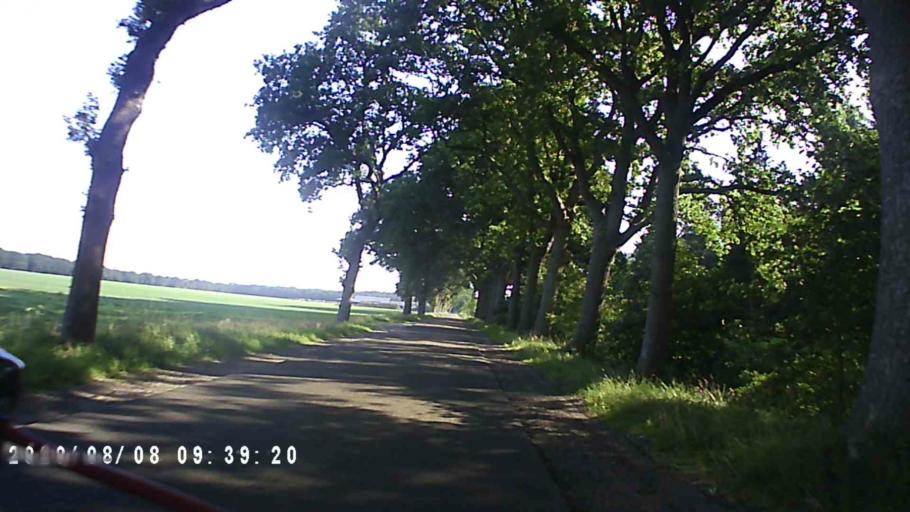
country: NL
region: Groningen
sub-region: Gemeente Leek
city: Leek
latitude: 53.0577
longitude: 6.3927
